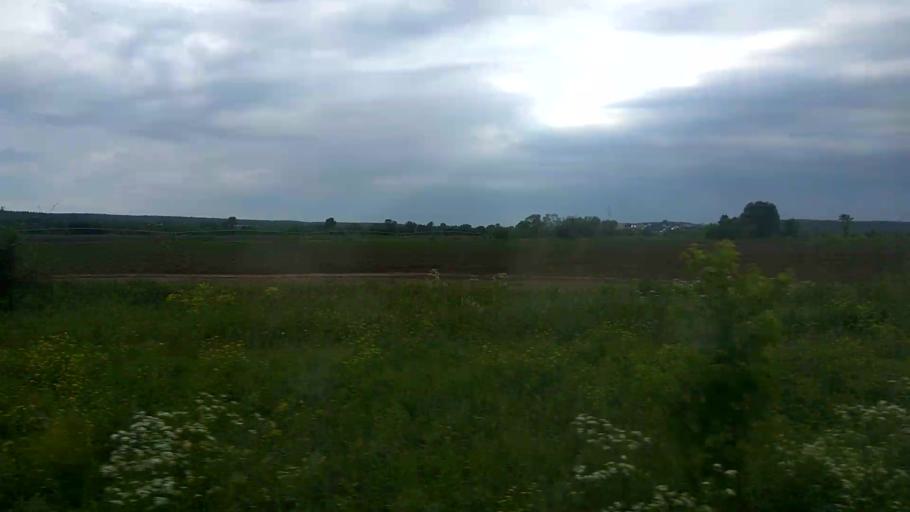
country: RU
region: Moskovskaya
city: Ozery
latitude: 54.8402
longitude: 38.5763
